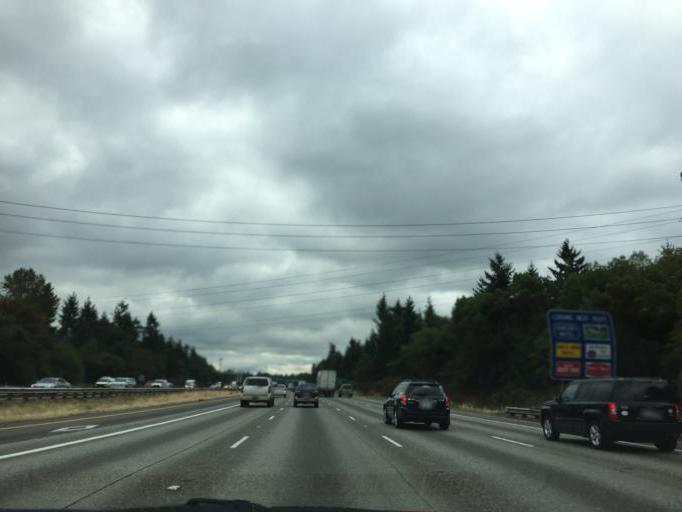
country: US
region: Washington
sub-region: King County
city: Des Moines
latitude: 47.4026
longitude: -122.2926
